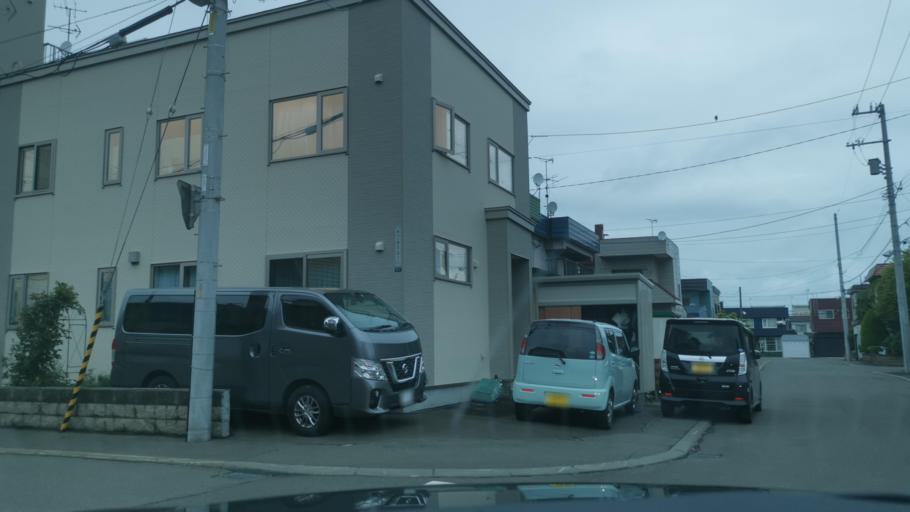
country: JP
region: Hokkaido
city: Sapporo
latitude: 43.1031
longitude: 141.3141
